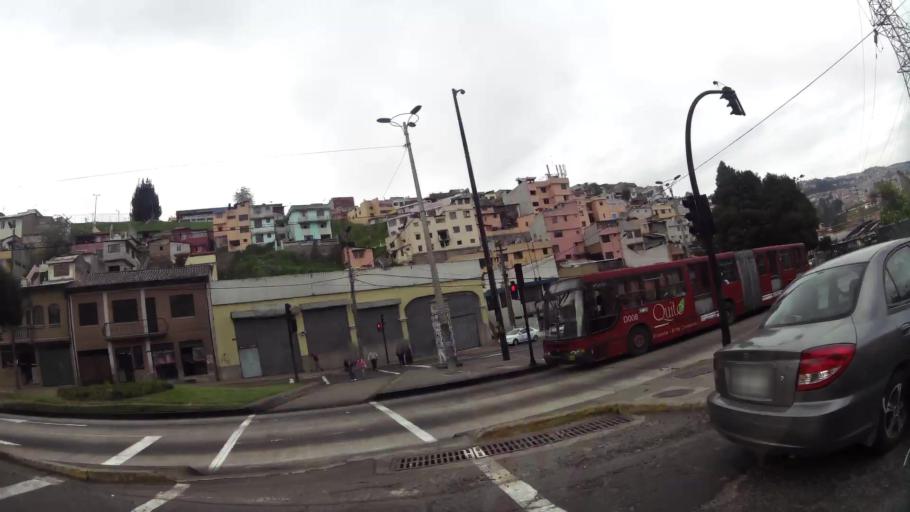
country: EC
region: Pichincha
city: Quito
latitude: -0.2270
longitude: -78.5069
